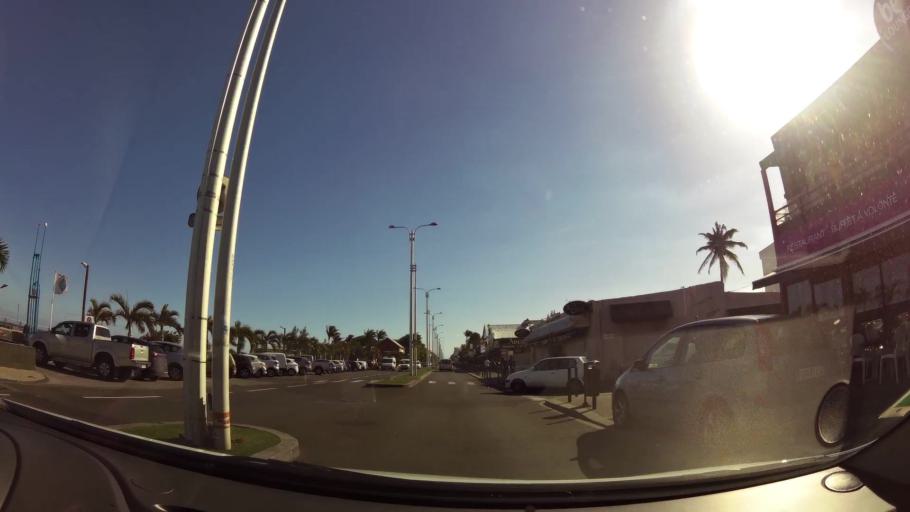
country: RE
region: Reunion
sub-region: Reunion
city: Saint-Pierre
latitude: -21.3436
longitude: 55.4757
